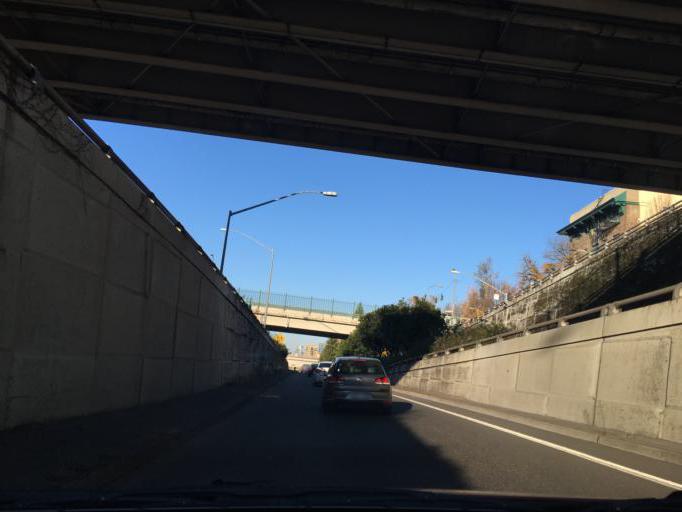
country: US
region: Oregon
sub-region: Multnomah County
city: Portland
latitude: 45.5162
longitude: -122.6879
